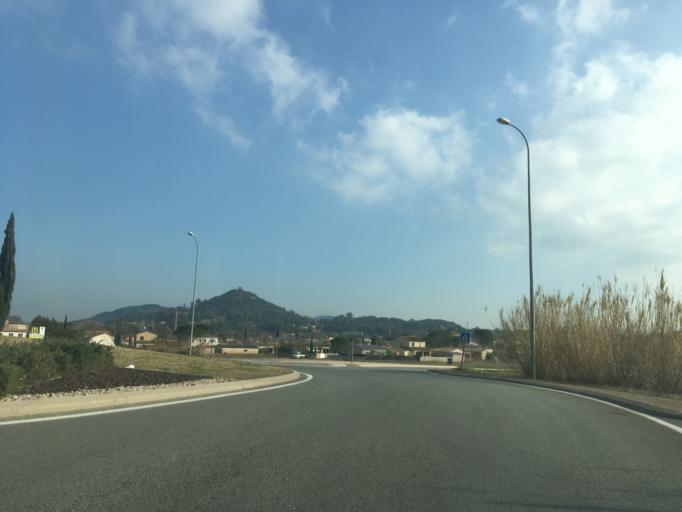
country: FR
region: Provence-Alpes-Cote d'Azur
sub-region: Departement du Var
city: Vidauban
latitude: 43.4141
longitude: 6.4188
